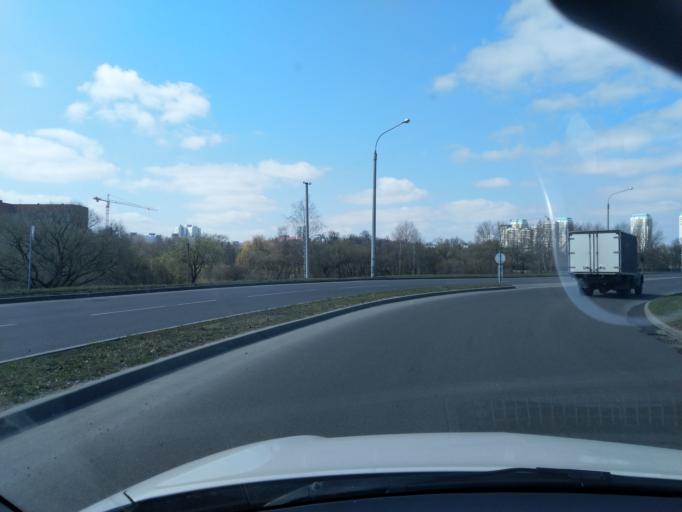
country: BY
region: Minsk
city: Syenitsa
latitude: 53.8638
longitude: 27.5016
